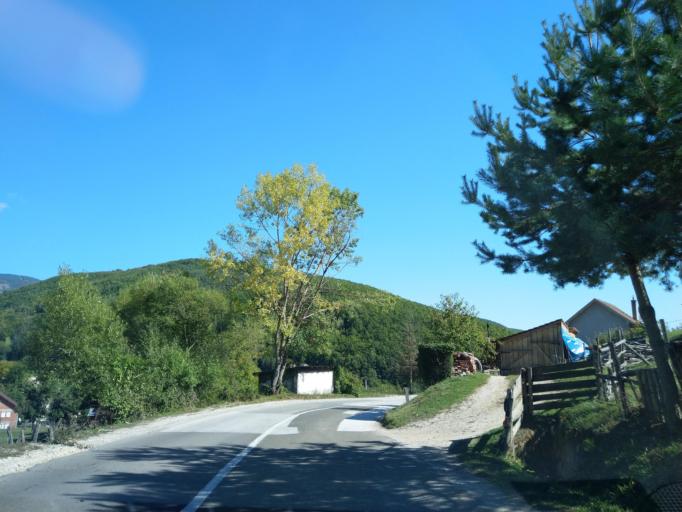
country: RS
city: Sokolovica
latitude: 43.2520
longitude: 20.2567
